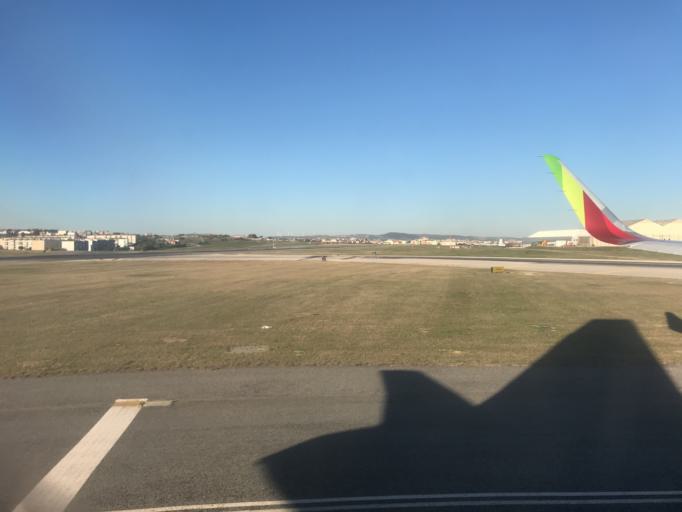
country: PT
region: Lisbon
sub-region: Loures
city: Camarate
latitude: 38.7837
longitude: -9.1331
